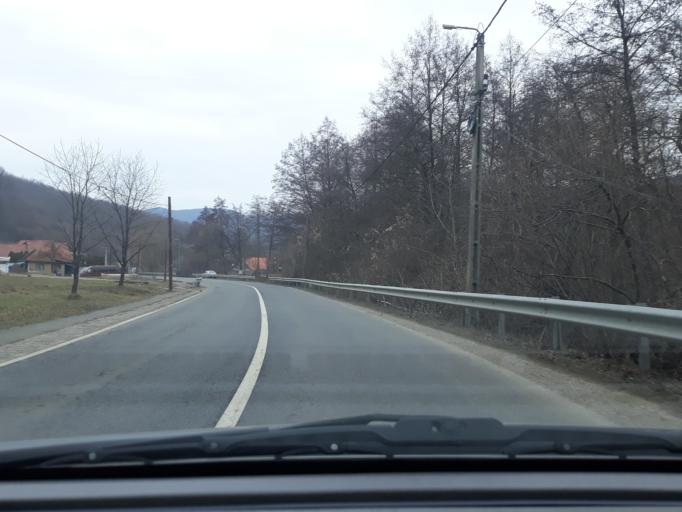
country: RO
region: Bihor
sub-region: Oras Alesd
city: Pestis
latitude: 47.0875
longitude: 22.4094
